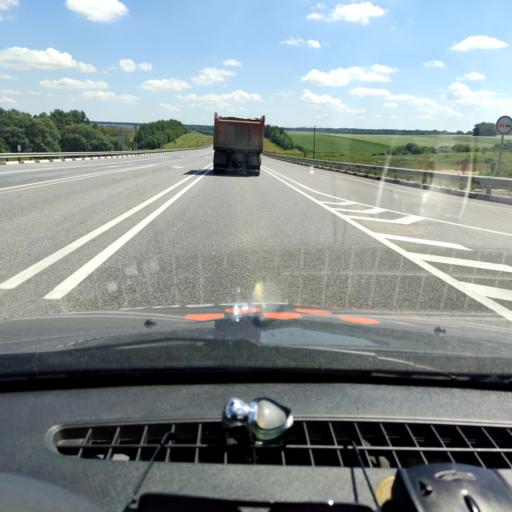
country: RU
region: Orjol
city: Zmiyevka
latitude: 52.8278
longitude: 36.2724
